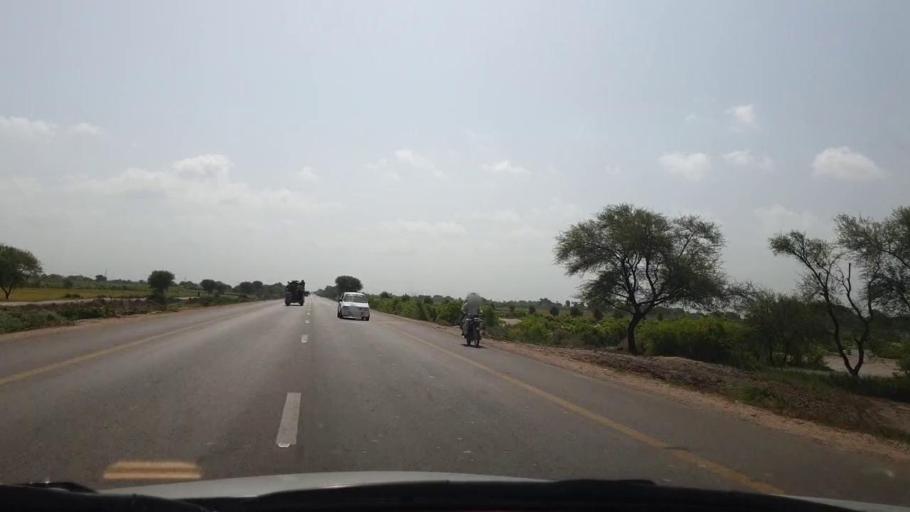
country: PK
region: Sindh
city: Matli
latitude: 24.9817
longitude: 68.6653
